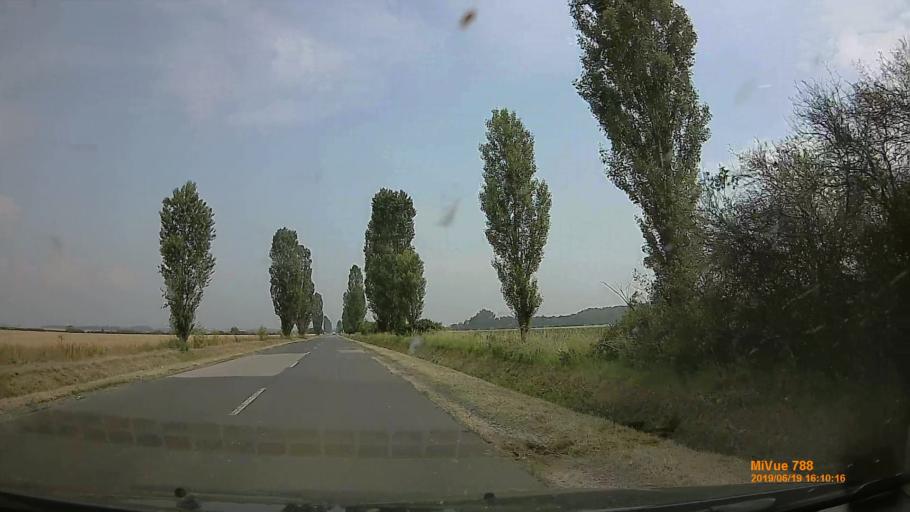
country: HU
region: Baranya
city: Szigetvar
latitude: 46.0712
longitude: 17.7659
